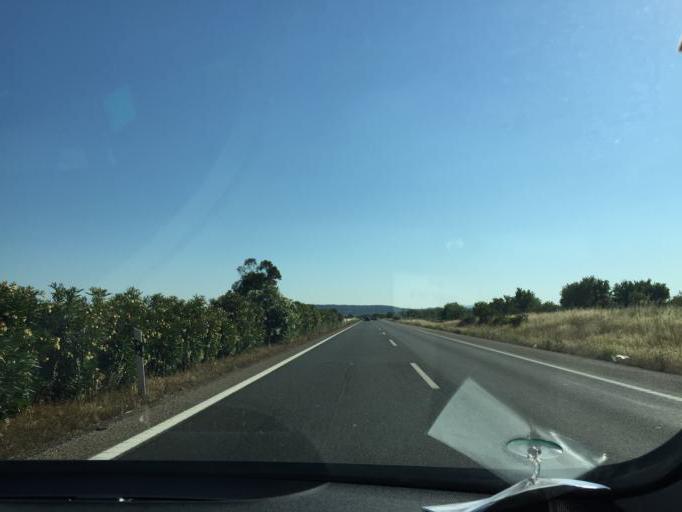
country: ES
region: Balearic Islands
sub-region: Illes Balears
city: Consell
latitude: 39.6627
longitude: 2.8126
